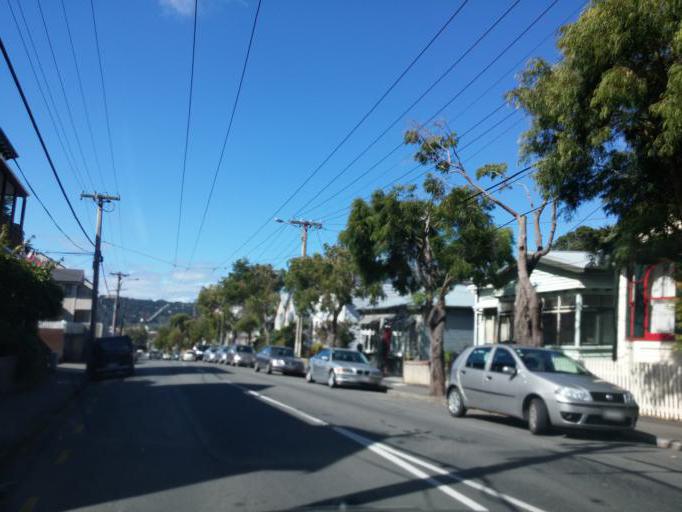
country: NZ
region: Wellington
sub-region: Wellington City
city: Kelburn
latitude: -41.2952
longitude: 174.7639
